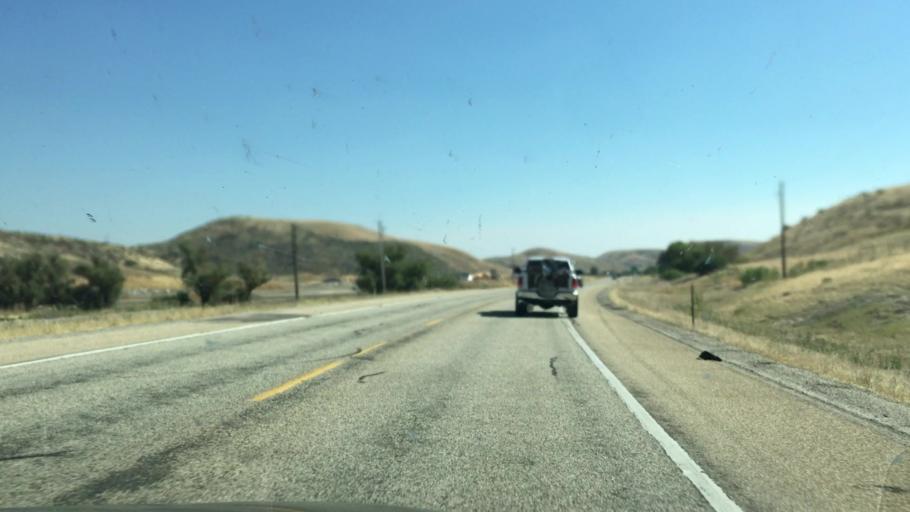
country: US
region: Idaho
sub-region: Ada County
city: Eagle
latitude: 43.7932
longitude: -116.2633
